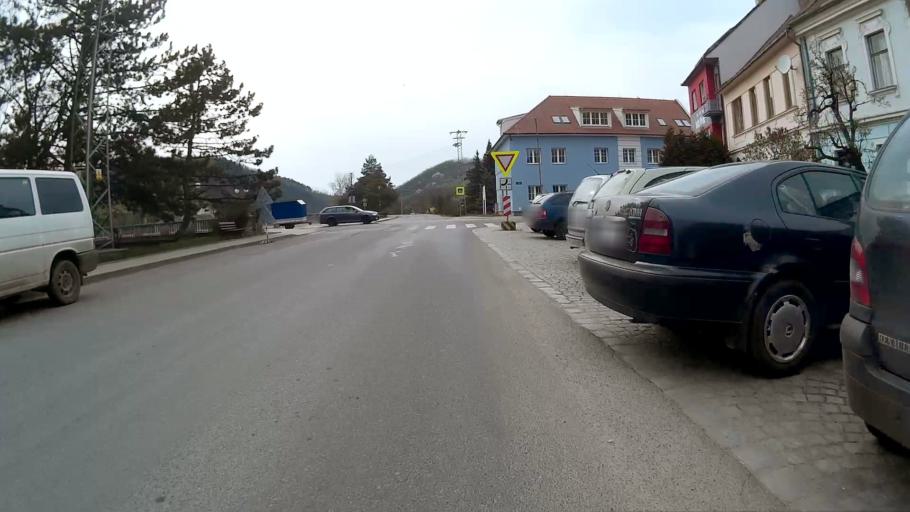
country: CZ
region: South Moravian
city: Dolni Kounice
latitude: 49.0720
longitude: 16.4650
